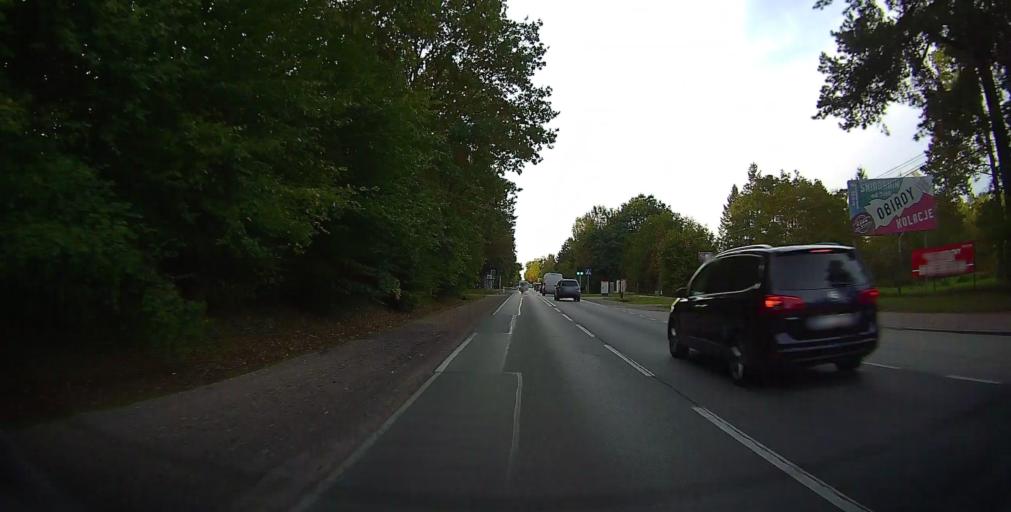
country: PL
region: Masovian Voivodeship
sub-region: Powiat piaseczynski
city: Zabieniec
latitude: 52.0515
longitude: 21.0632
